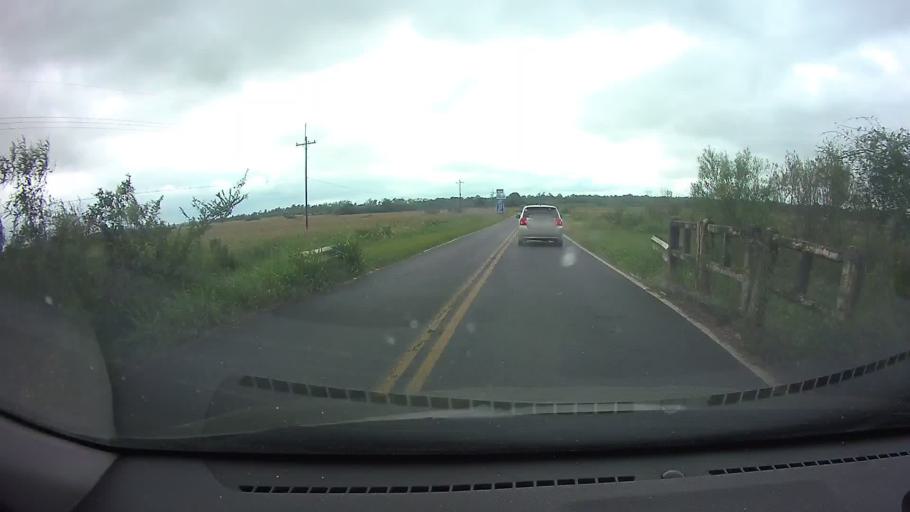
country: PY
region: Central
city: Nueva Italia
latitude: -25.5597
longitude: -57.5011
